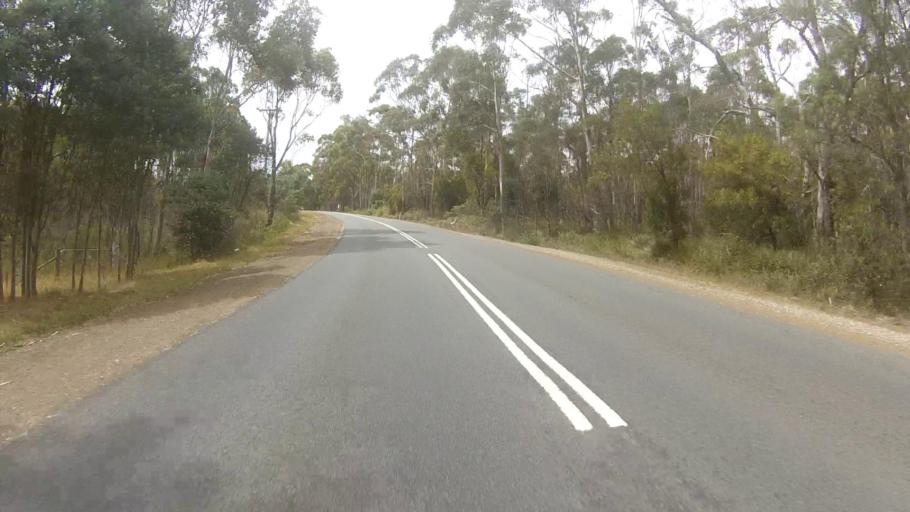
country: AU
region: Tasmania
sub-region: Kingborough
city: Margate
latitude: -42.9962
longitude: 147.2224
